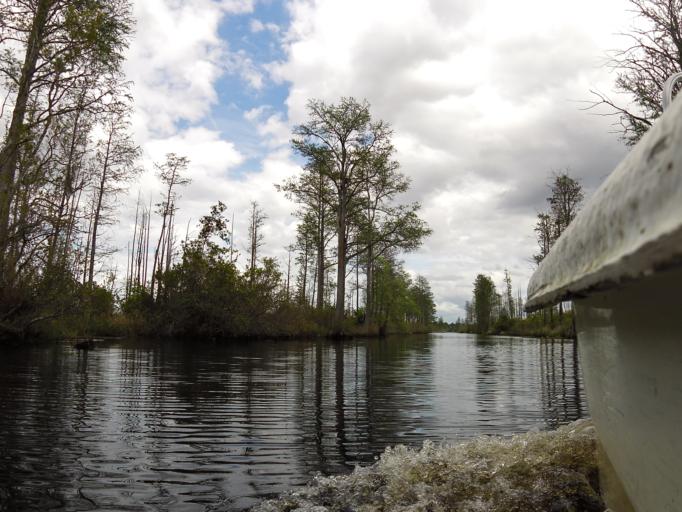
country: US
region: Georgia
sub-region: Charlton County
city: Folkston
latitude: 30.7352
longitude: -82.1555
